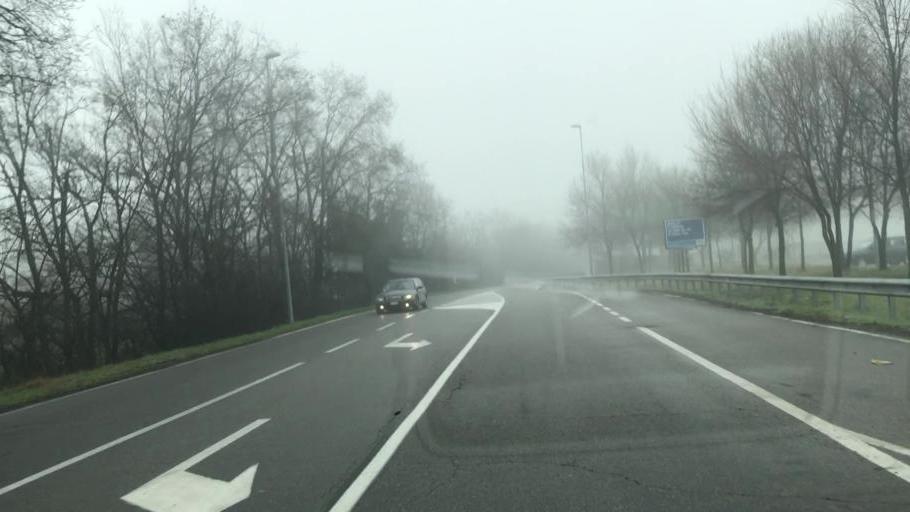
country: IT
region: Lombardy
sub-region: Provincia di Brescia
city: Montichiari
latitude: 45.3906
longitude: 10.4035
